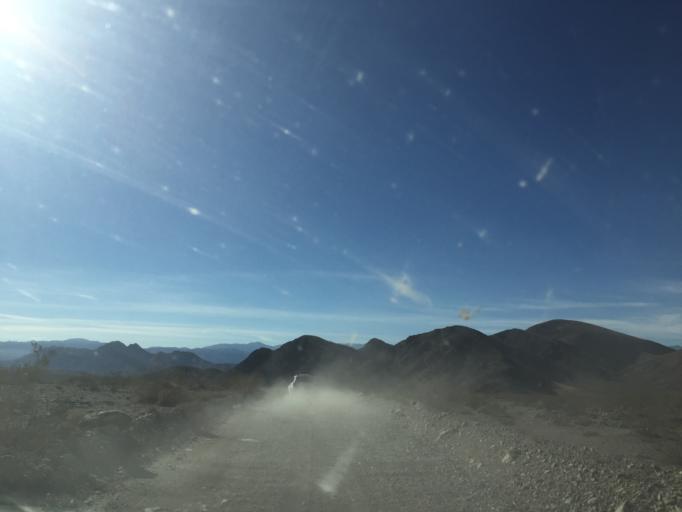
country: US
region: California
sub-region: Inyo County
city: Lone Pine
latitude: 36.7820
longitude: -117.5250
